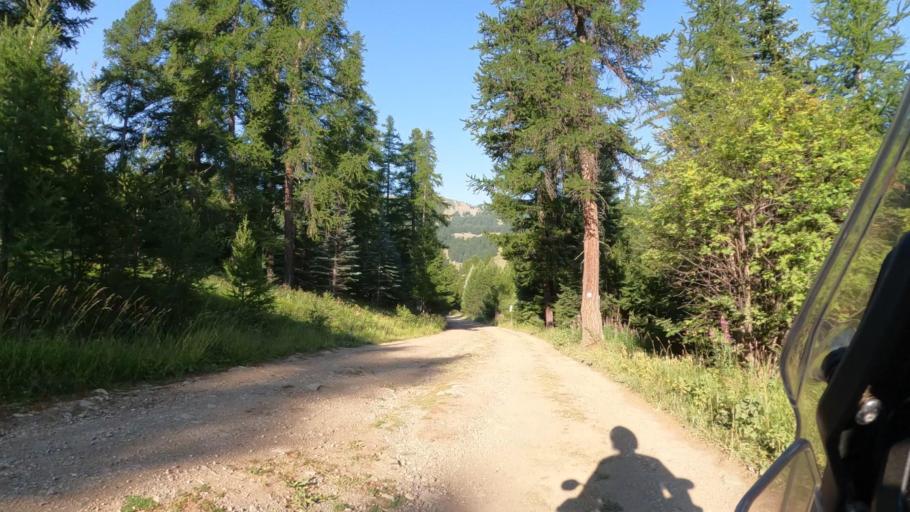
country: FR
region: Provence-Alpes-Cote d'Azur
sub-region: Departement des Hautes-Alpes
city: Guillestre
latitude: 44.6211
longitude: 6.6406
